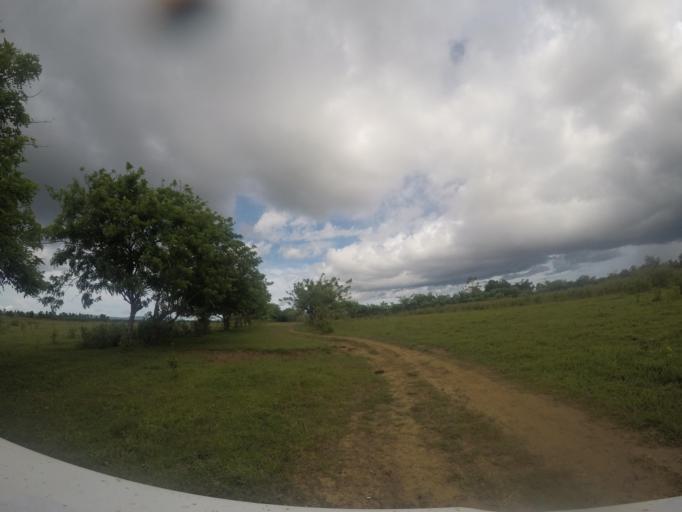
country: TL
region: Lautem
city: Lospalos
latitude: -8.5065
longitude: 127.0162
